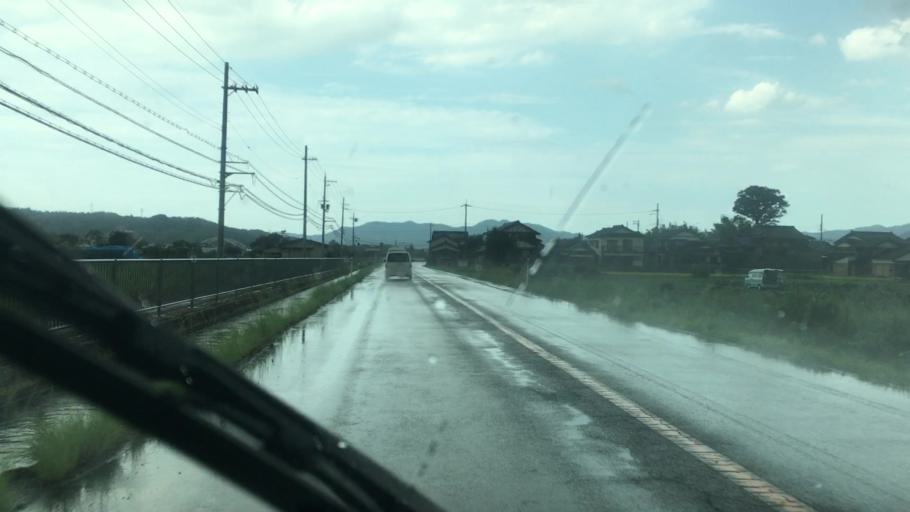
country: JP
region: Hyogo
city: Toyooka
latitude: 35.4953
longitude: 134.8162
